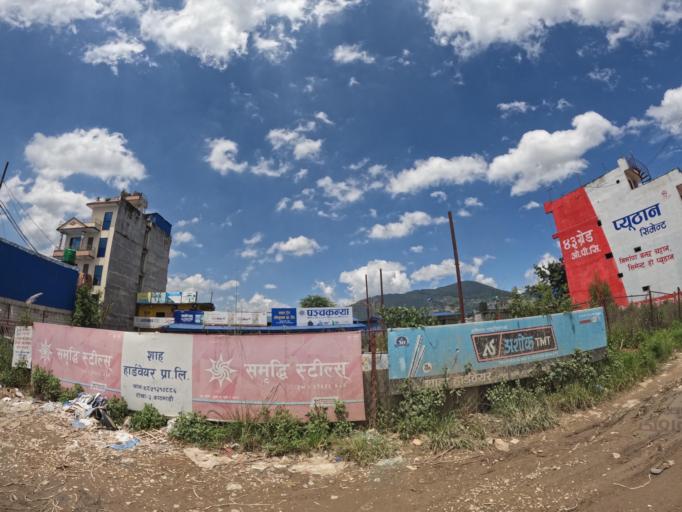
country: NP
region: Central Region
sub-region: Bagmati Zone
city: Kathmandu
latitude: 27.7598
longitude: 85.3289
